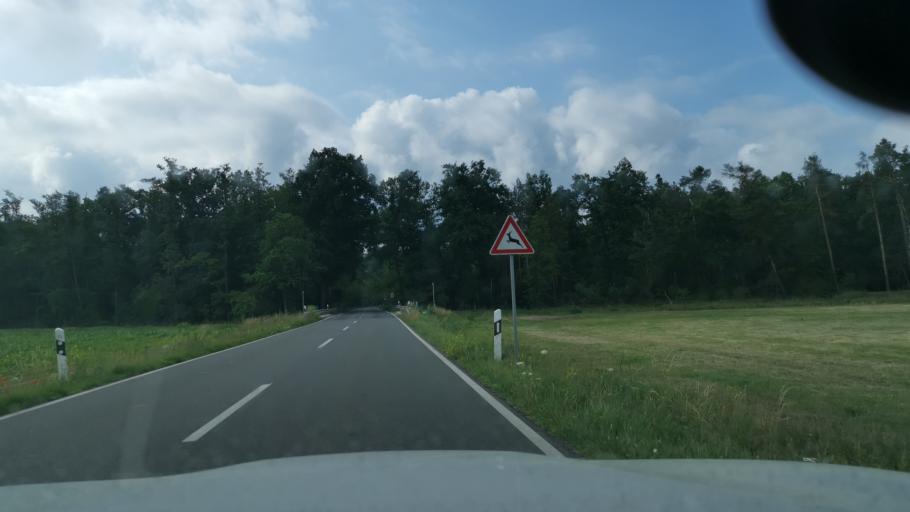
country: DE
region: Saxony-Anhalt
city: Annaburg
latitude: 51.7577
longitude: 13.0392
